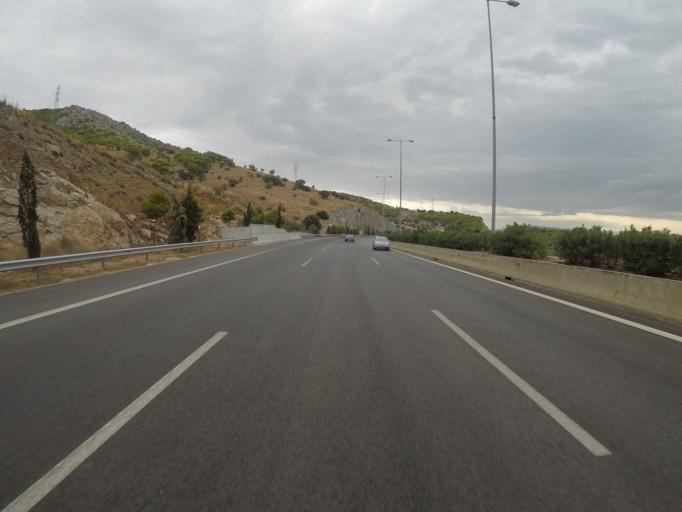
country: GR
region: Attica
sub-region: Nomarchia Dytikis Attikis
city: Vlychada
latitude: 38.0304
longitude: 23.4720
